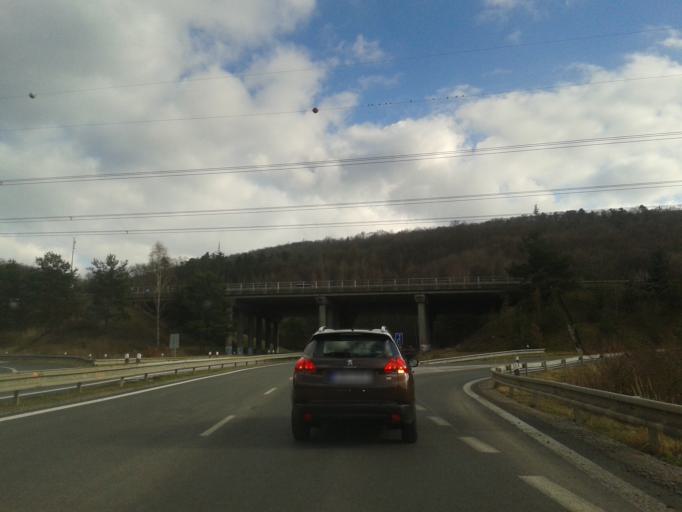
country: CZ
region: Central Bohemia
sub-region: Okres Beroun
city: Beroun
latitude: 49.9757
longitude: 14.1070
